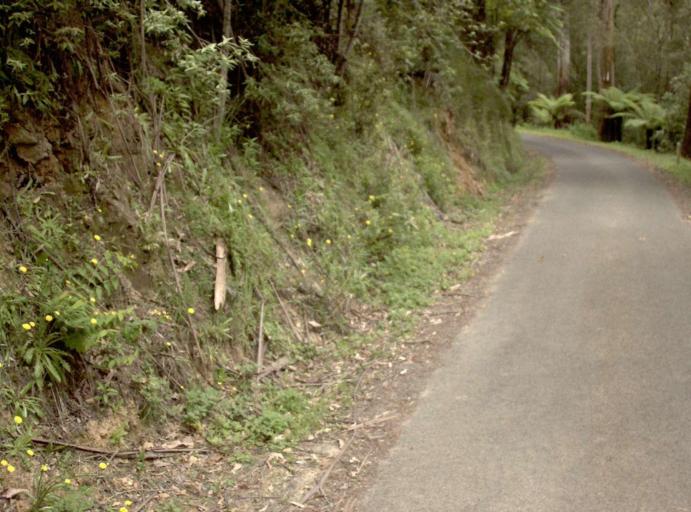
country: AU
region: Victoria
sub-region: Latrobe
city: Traralgon
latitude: -38.4614
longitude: 146.5482
